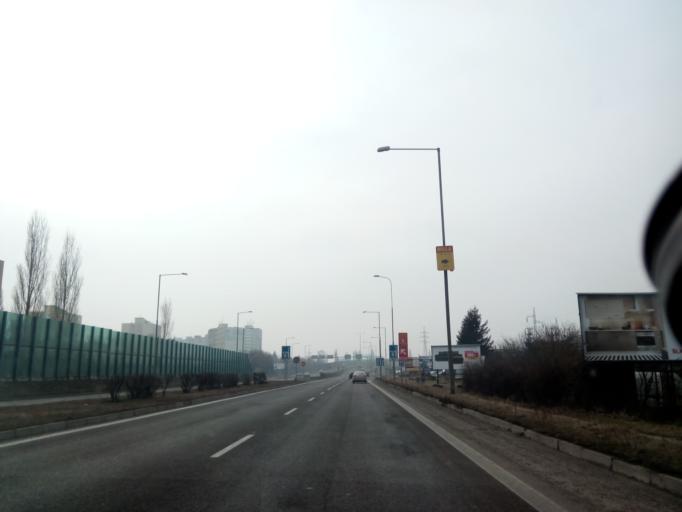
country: SK
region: Kosicky
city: Kosice
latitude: 48.6953
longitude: 21.2801
